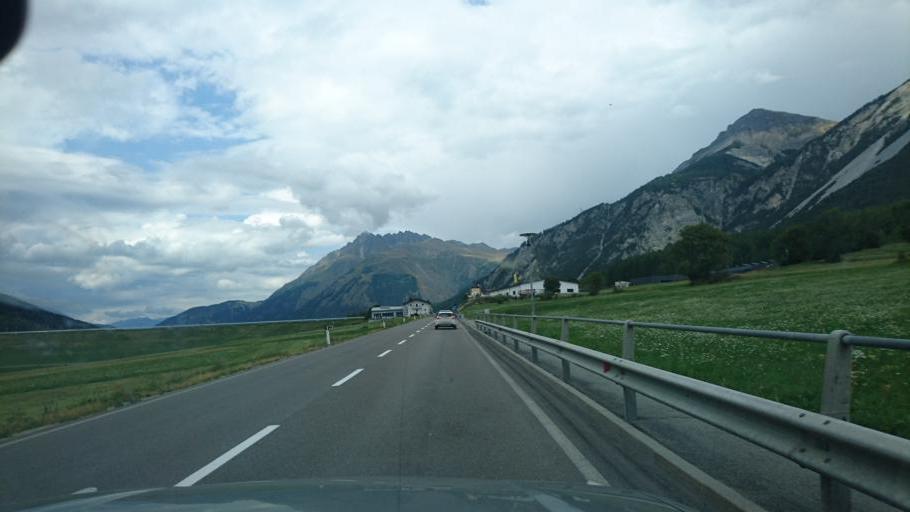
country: IT
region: Trentino-Alto Adige
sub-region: Bolzano
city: Curon Venosta
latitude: 46.7704
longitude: 10.5337
